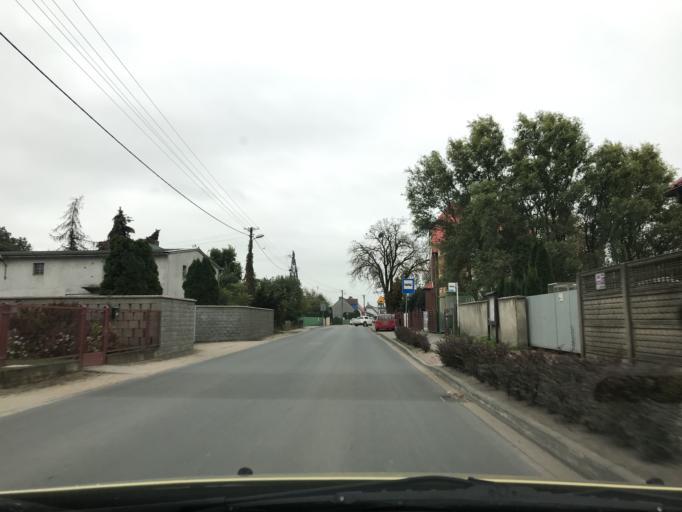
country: PL
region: Greater Poland Voivodeship
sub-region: Powiat poznanski
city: Baranowo
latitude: 52.4041
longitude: 16.7395
